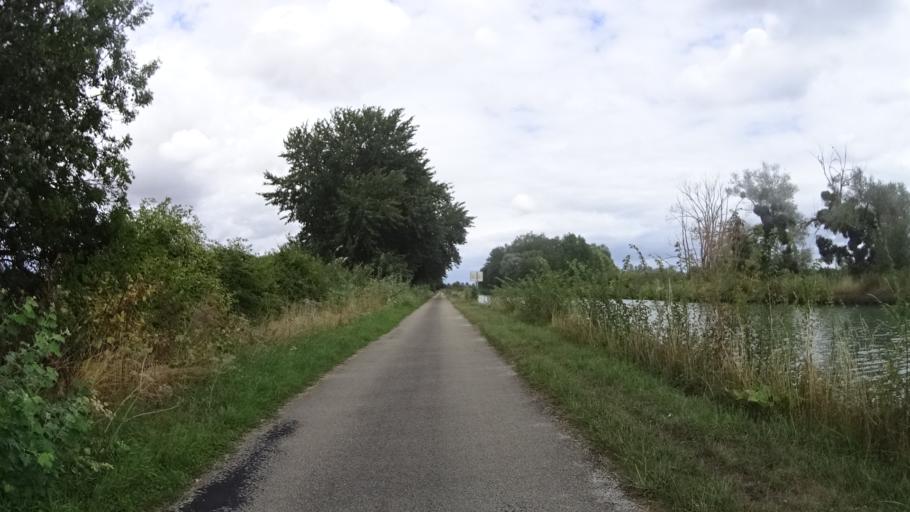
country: FR
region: Picardie
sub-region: Departement de l'Aisne
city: Tergnier
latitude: 49.6467
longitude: 3.2969
